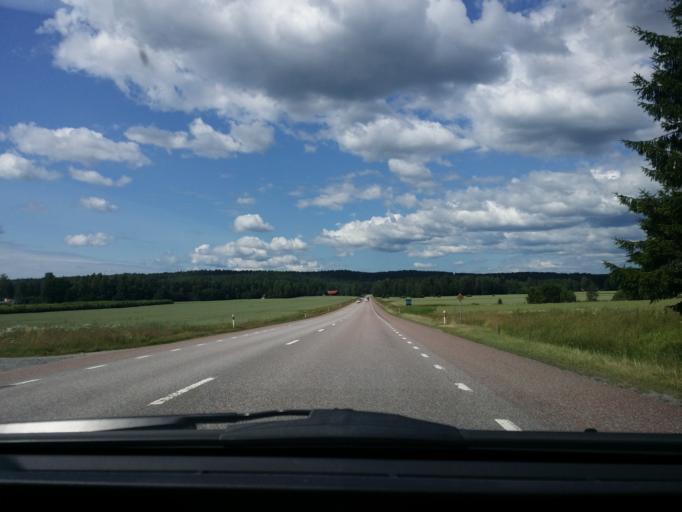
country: SE
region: OErebro
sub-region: Orebro Kommun
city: Hovsta
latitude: 59.4360
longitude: 15.1587
